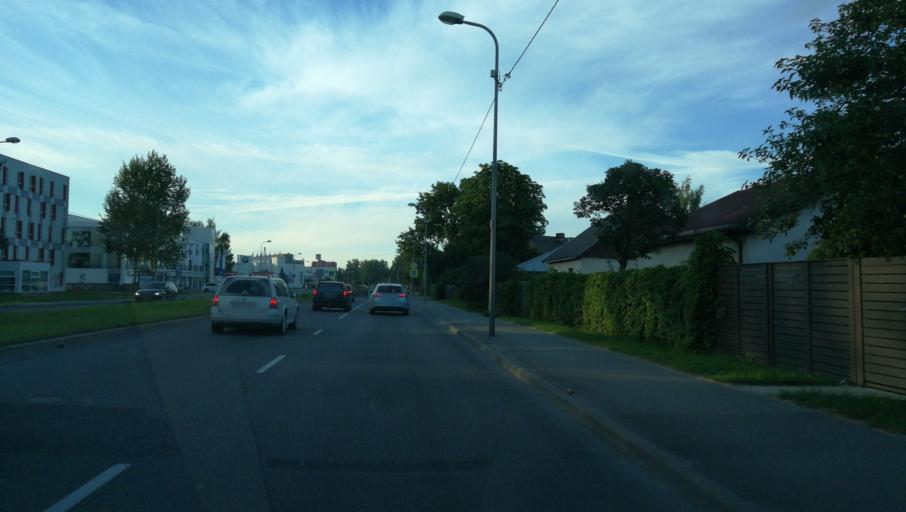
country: LV
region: Riga
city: Riga
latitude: 56.9367
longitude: 24.1825
